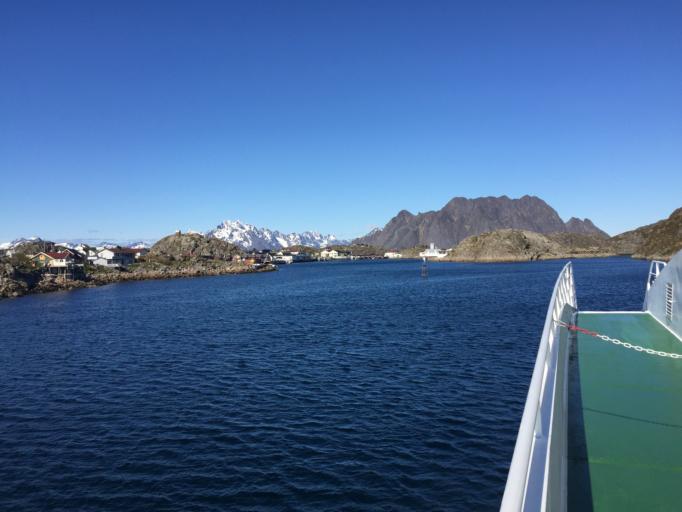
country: NO
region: Nordland
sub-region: Vagan
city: Svolvaer
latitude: 68.1607
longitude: 14.6541
